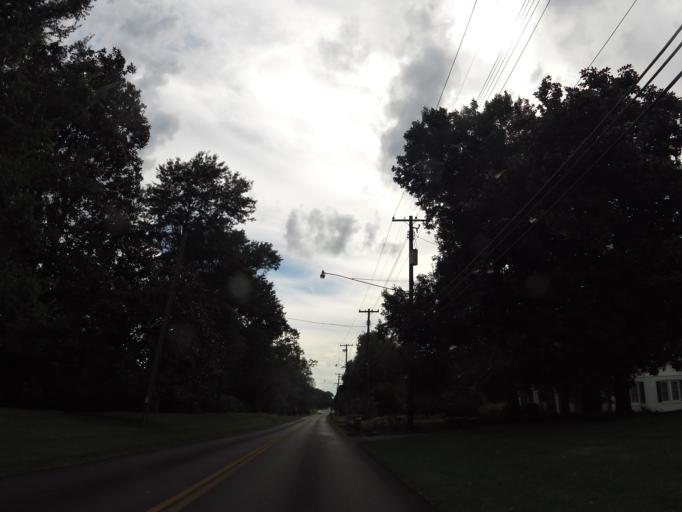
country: US
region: Kentucky
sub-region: Christian County
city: Hopkinsville
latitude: 36.8500
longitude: -87.5086
